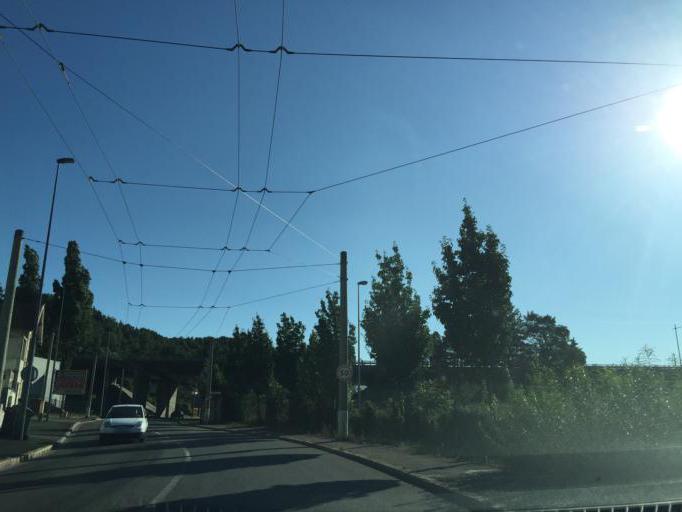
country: FR
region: Rhone-Alpes
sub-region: Departement de la Loire
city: Saint-Jean-Bonnefonds
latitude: 45.4417
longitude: 4.4331
